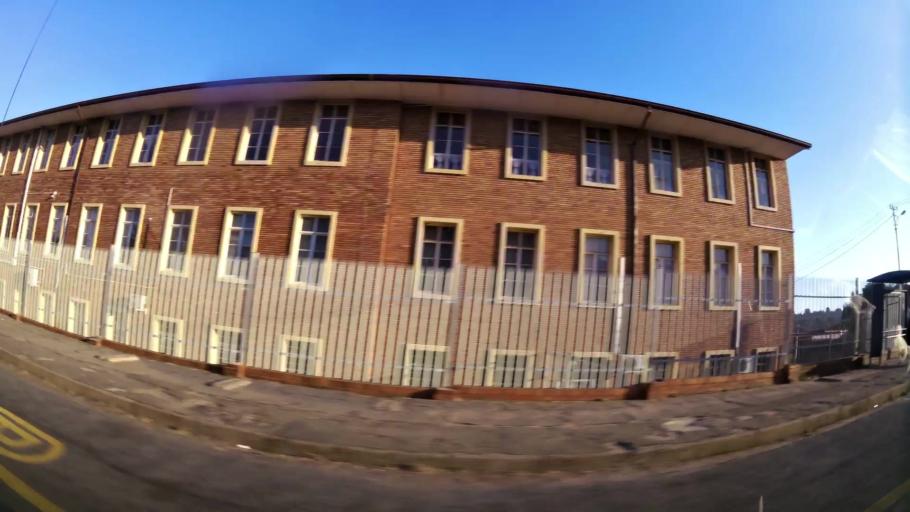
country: ZA
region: Gauteng
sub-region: City of Johannesburg Metropolitan Municipality
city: Roodepoort
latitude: -26.1666
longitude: 27.8937
